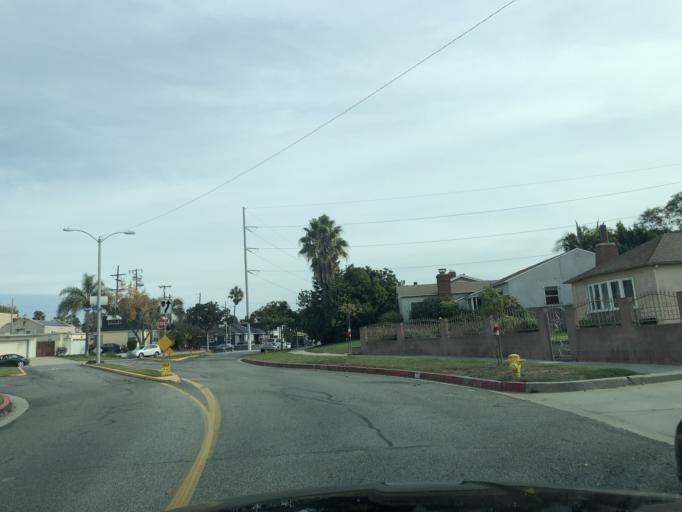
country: US
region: California
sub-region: Los Angeles County
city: Ladera Heights
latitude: 33.9812
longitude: -118.3613
